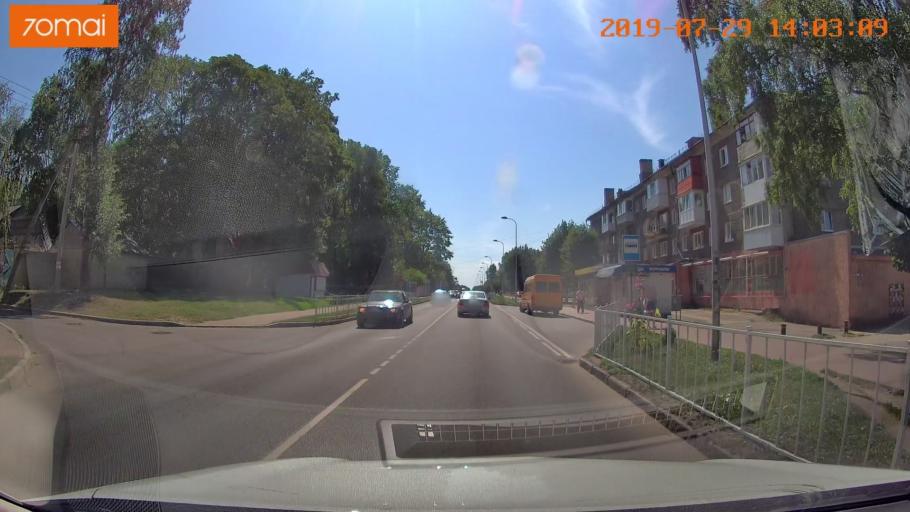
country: RU
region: Kaliningrad
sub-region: Gorod Kaliningrad
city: Baltiysk
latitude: 54.6596
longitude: 19.9143
